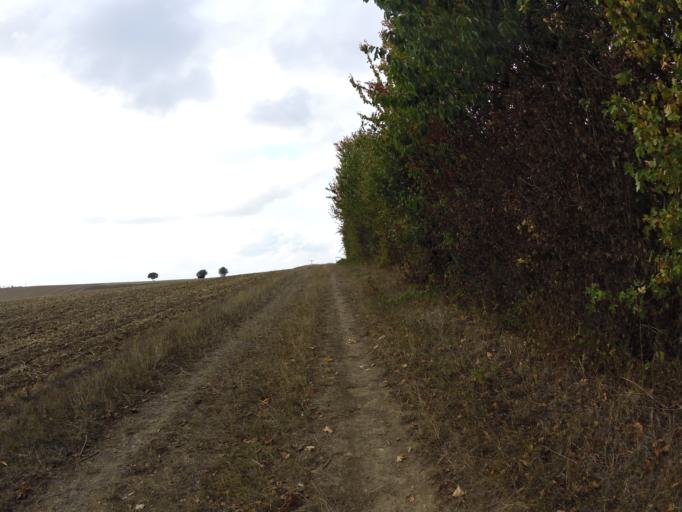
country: DE
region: Bavaria
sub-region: Regierungsbezirk Unterfranken
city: Eisingen
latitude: 49.7519
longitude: 9.8286
